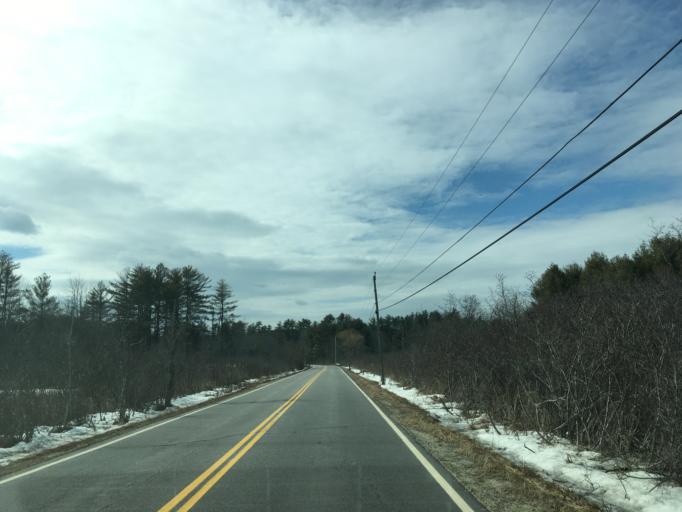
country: US
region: New Hampshire
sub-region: Rockingham County
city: North Hampton
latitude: 42.9951
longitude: -70.8628
